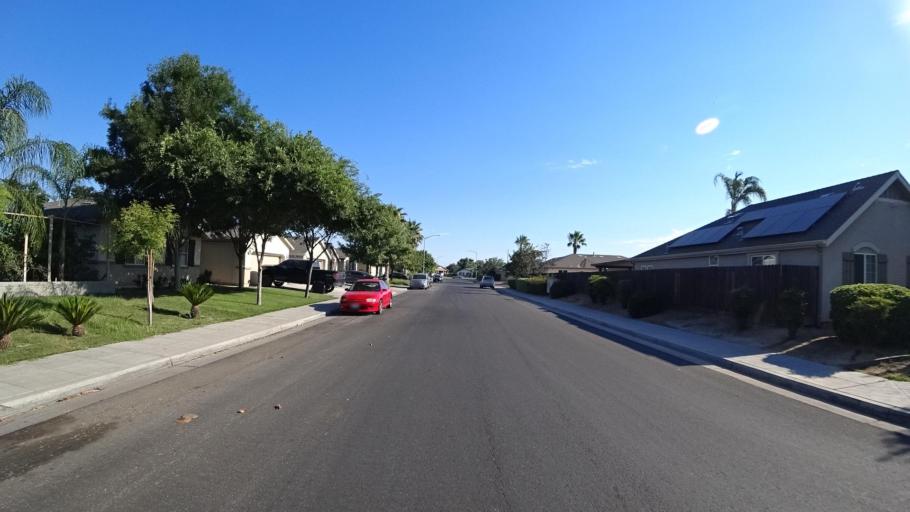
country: US
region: California
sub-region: Fresno County
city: Fresno
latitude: 36.7124
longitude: -119.7496
